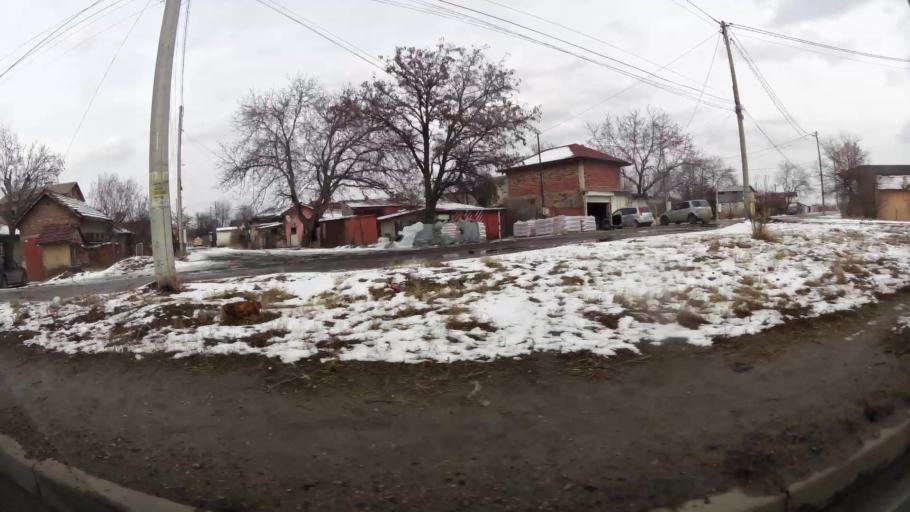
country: BG
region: Sofia-Capital
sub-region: Stolichna Obshtina
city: Sofia
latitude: 42.6916
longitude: 23.3859
